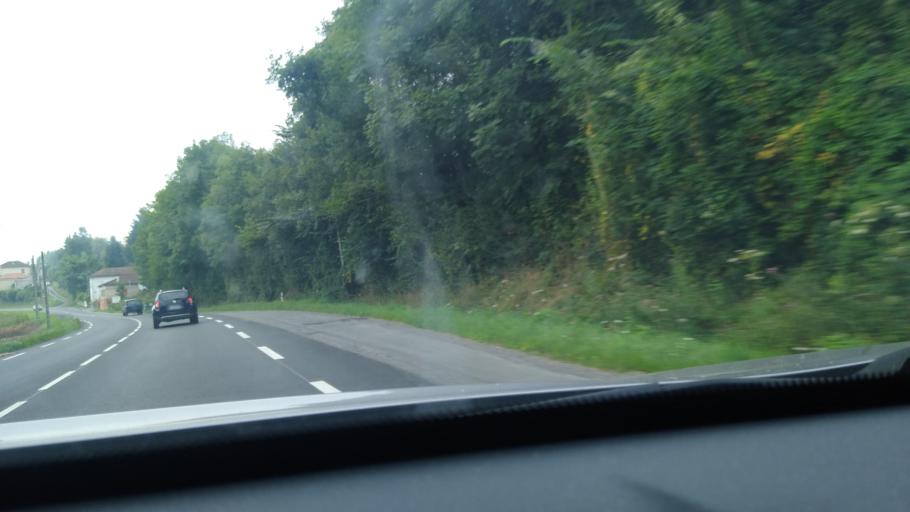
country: FR
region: Midi-Pyrenees
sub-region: Departement de la Haute-Garonne
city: Salies-du-Salat
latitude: 43.0708
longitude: 0.9664
